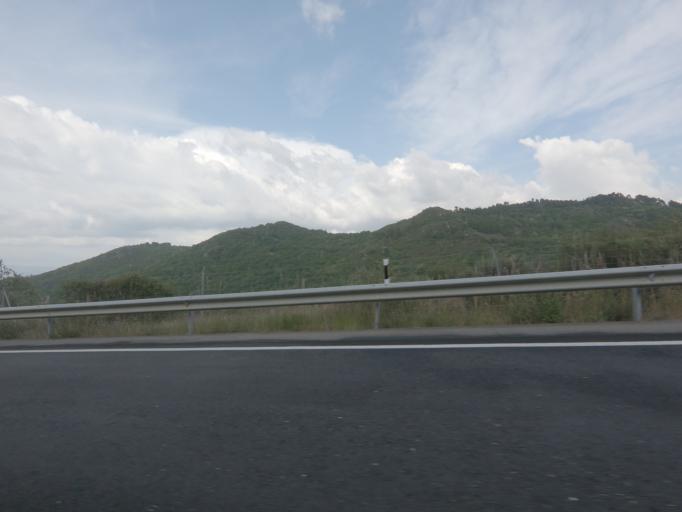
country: ES
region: Galicia
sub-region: Provincia de Ourense
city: Ambia
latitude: 42.1767
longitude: -7.7636
